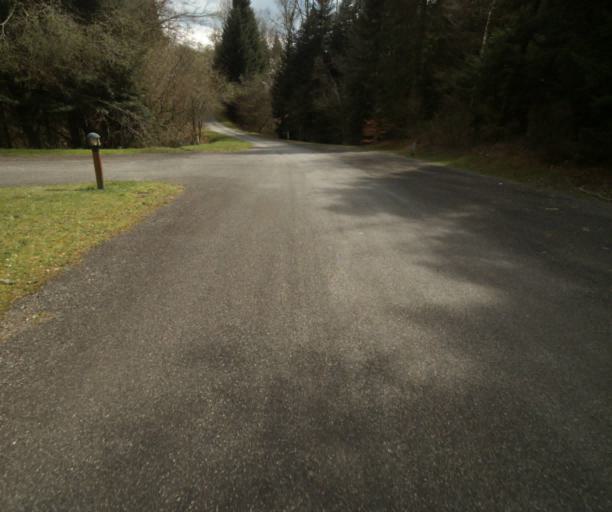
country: FR
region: Limousin
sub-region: Departement de la Correze
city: Correze
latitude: 45.2924
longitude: 1.9524
